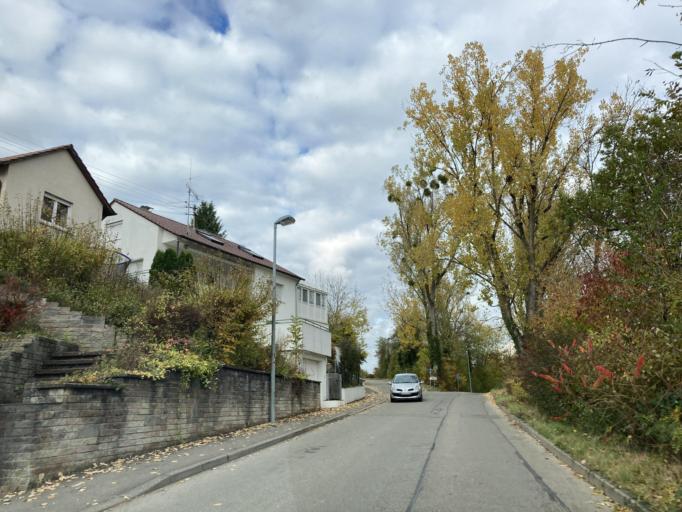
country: DE
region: Baden-Wuerttemberg
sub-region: Tuebingen Region
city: Dusslingen
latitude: 48.4558
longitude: 9.0554
